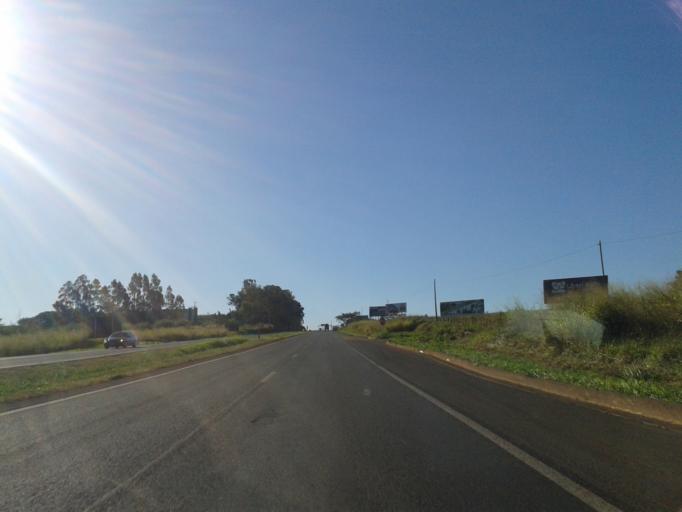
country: BR
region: Minas Gerais
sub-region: Uberlandia
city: Uberlandia
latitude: -18.9860
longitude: -48.2120
